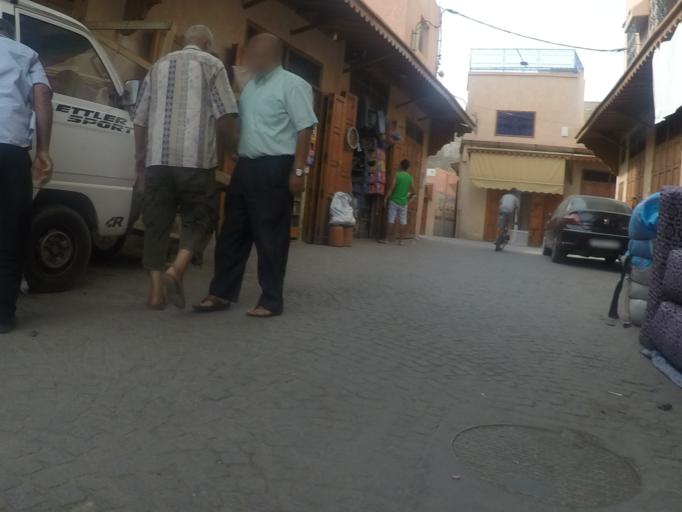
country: MA
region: Marrakech-Tensift-Al Haouz
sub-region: Marrakech
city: Marrakesh
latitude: 31.6296
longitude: -7.9832
